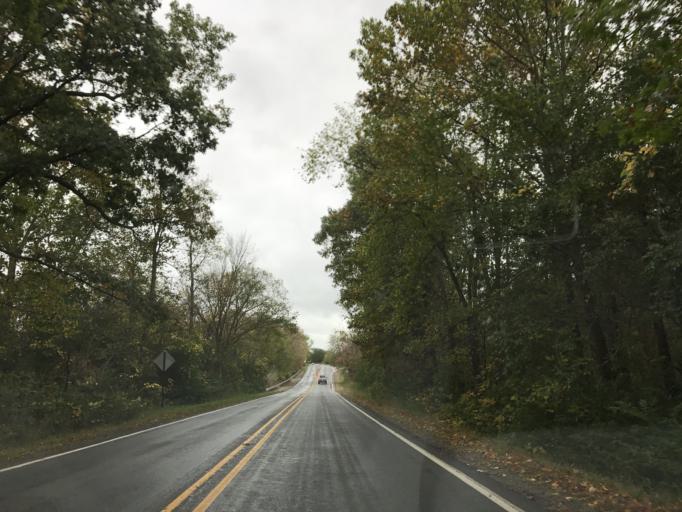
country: US
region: Michigan
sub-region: Washtenaw County
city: Ypsilanti
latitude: 42.3091
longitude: -83.6618
